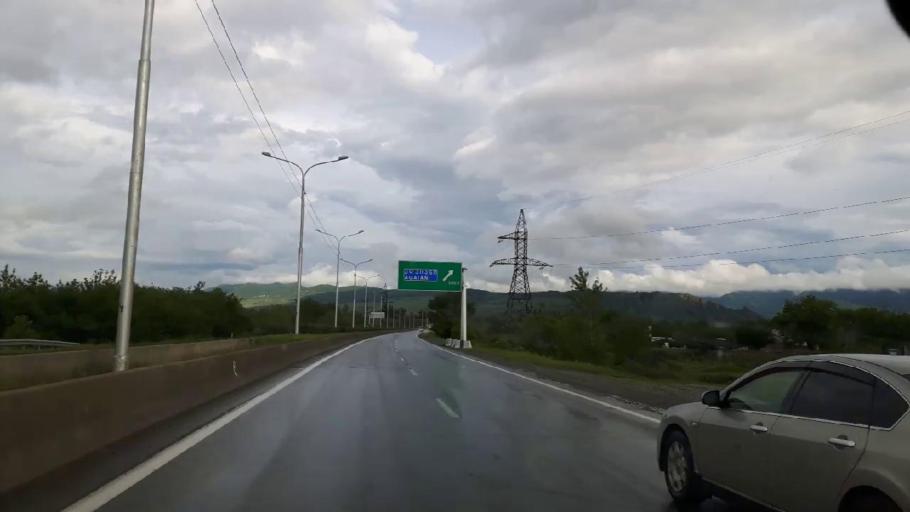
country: GE
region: Shida Kartli
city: Kaspi
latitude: 41.9168
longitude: 44.5535
